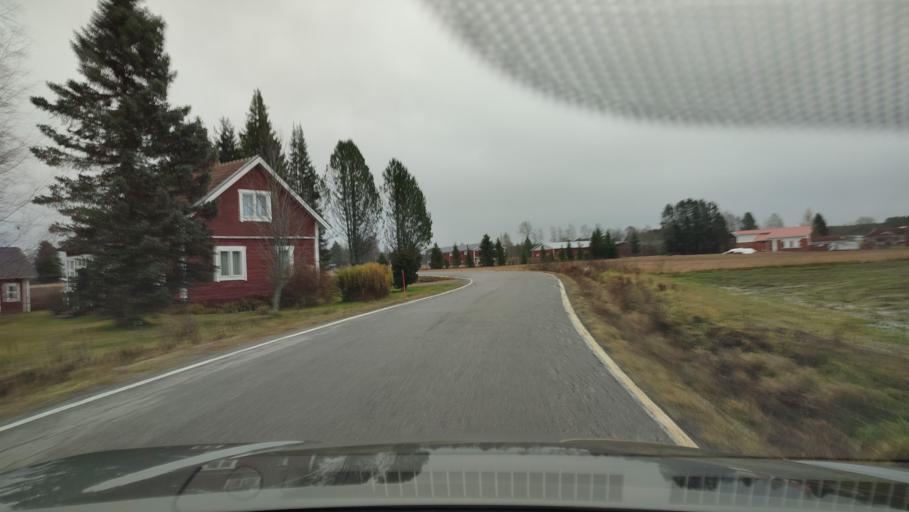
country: FI
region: Southern Ostrobothnia
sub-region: Suupohja
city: Isojoki
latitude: 62.1911
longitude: 21.9748
